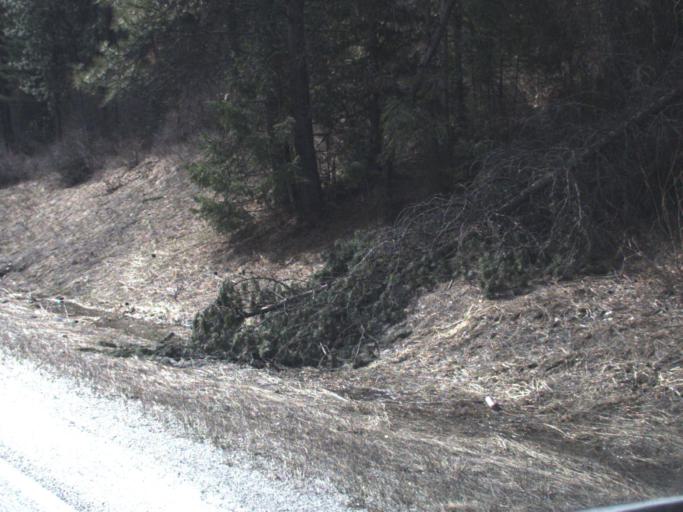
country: US
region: Washington
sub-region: Pend Oreille County
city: Newport
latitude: 48.4021
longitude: -117.3141
